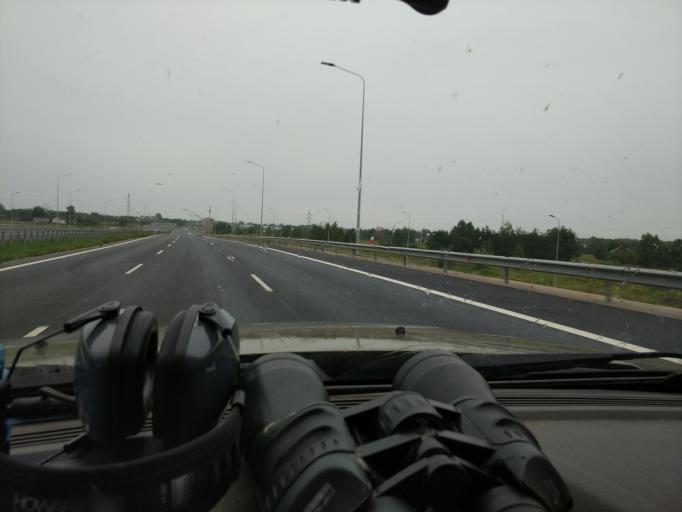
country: PL
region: Masovian Voivodeship
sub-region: Powiat wolominski
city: Radzymin
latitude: 52.3988
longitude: 21.2016
